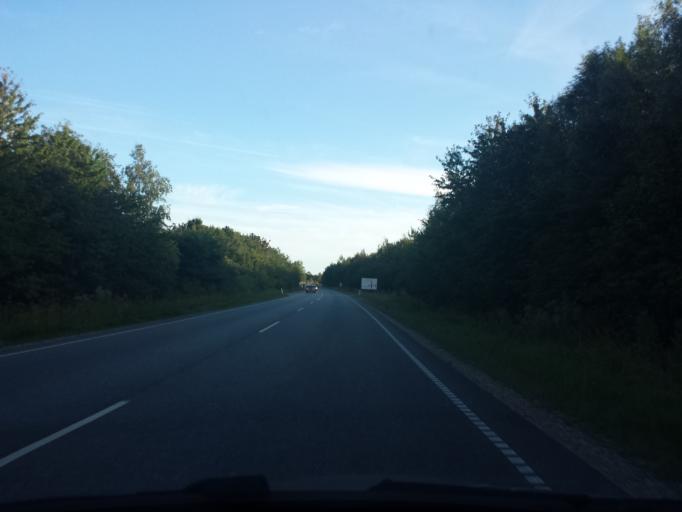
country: DK
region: Capital Region
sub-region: Frederikssund Kommune
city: Frederikssund
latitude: 55.8077
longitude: 12.1021
